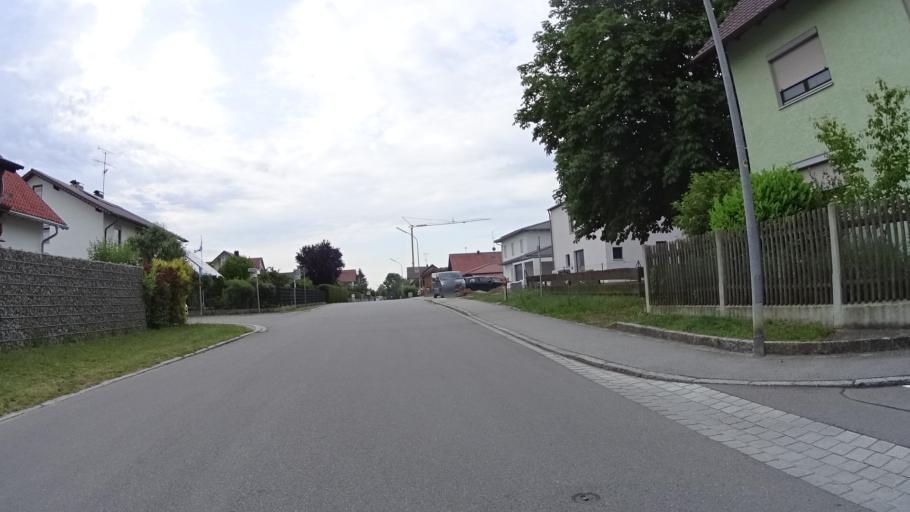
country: DE
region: Bavaria
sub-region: Lower Bavaria
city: Kirchroth
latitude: 48.9290
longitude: 12.5518
